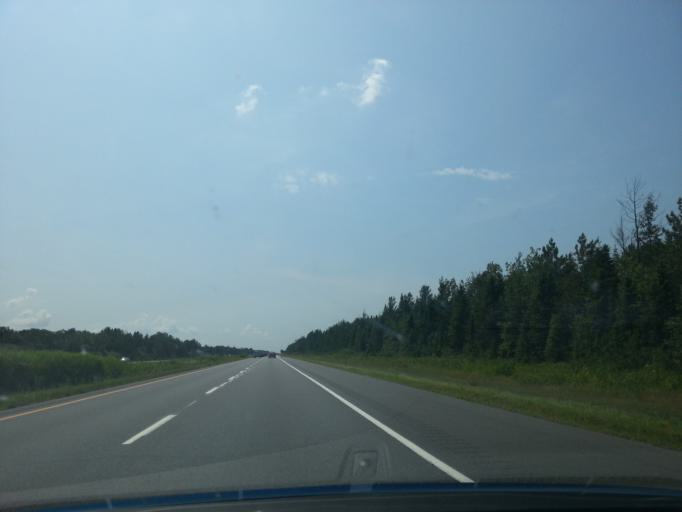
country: CA
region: Quebec
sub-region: Mauricie
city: Princeville
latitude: 46.2871
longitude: -71.9872
